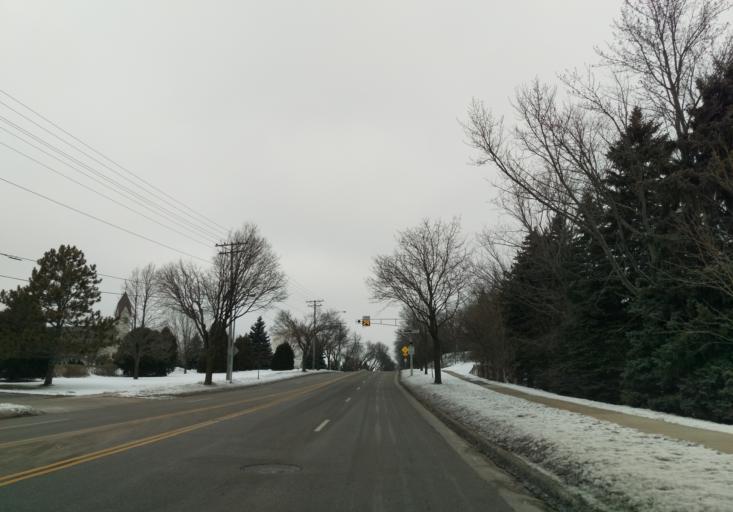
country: US
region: Wisconsin
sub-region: Dane County
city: Middleton
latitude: 43.0687
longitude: -89.5025
